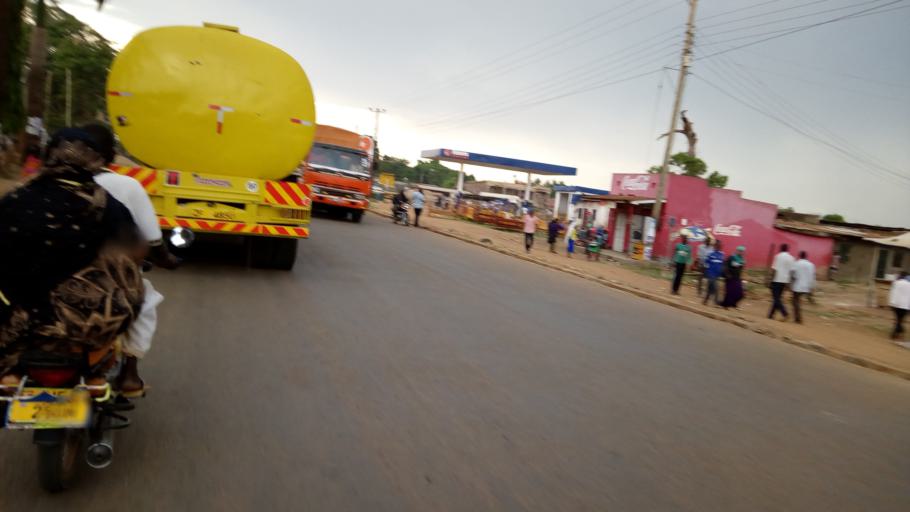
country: UG
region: Eastern Region
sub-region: Mbale District
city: Mbale
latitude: 1.0915
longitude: 34.1770
